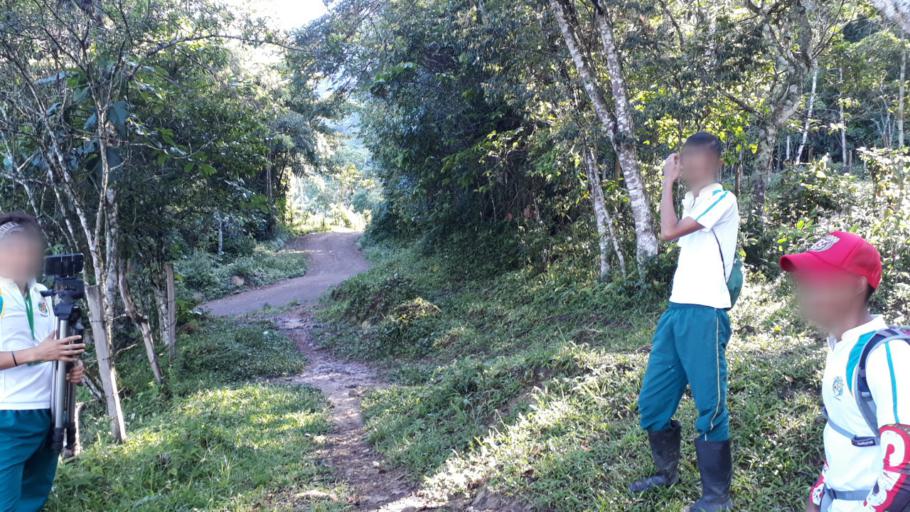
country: CO
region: Casanare
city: Nunchia
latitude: 5.6423
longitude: -72.4248
